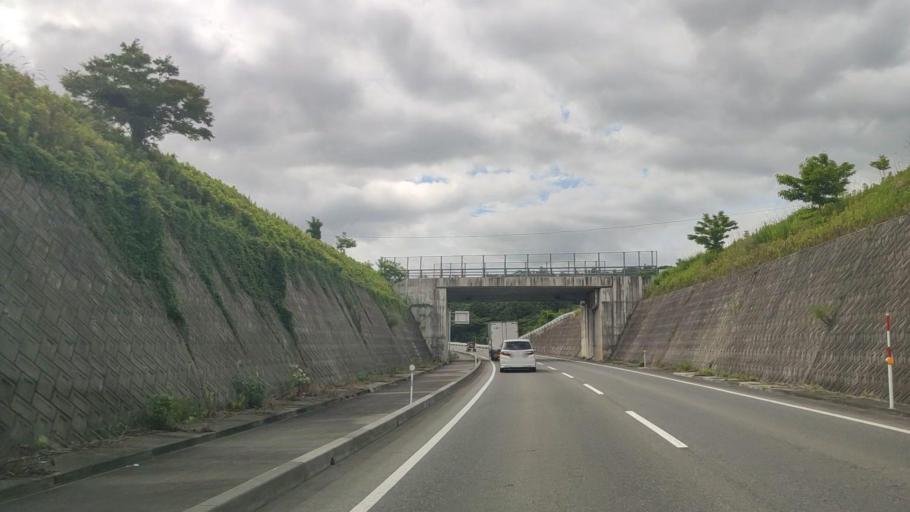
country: JP
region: Tottori
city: Yonago
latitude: 35.3818
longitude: 133.3877
